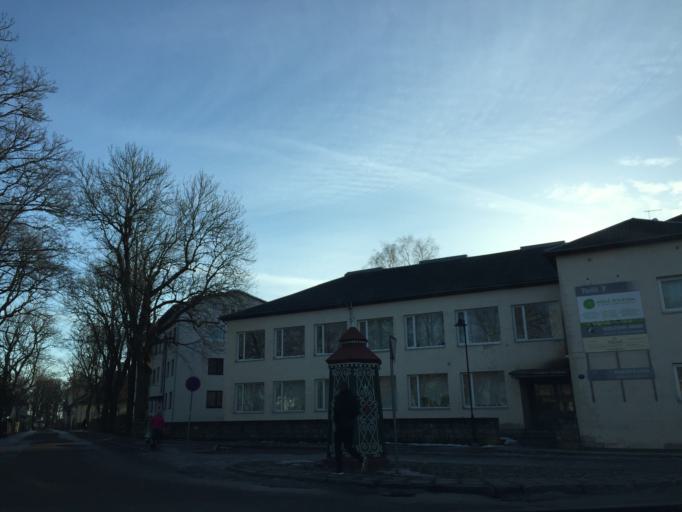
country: EE
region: Saare
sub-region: Kuressaare linn
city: Kuressaare
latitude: 58.2522
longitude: 22.4796
